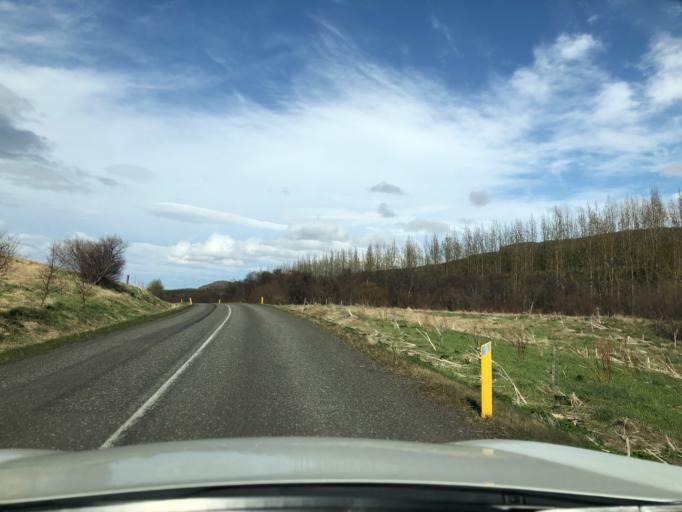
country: IS
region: East
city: Egilsstadir
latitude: 65.1050
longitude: -14.7233
